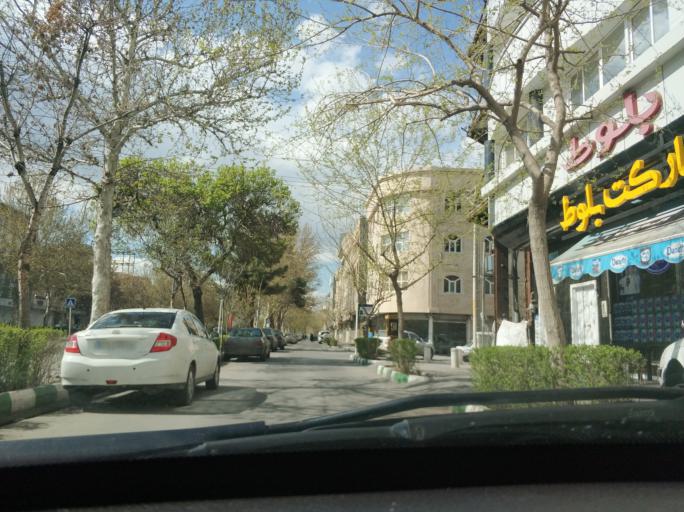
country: IR
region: Razavi Khorasan
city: Mashhad
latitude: 36.2695
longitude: 59.5975
